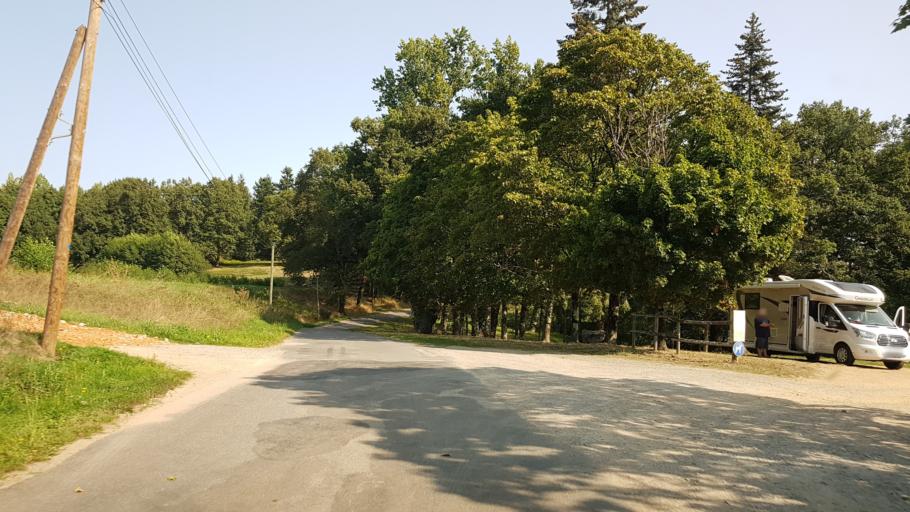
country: FR
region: Poitou-Charentes
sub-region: Departement de la Charente
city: Etagnac
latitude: 45.8999
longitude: 0.7741
